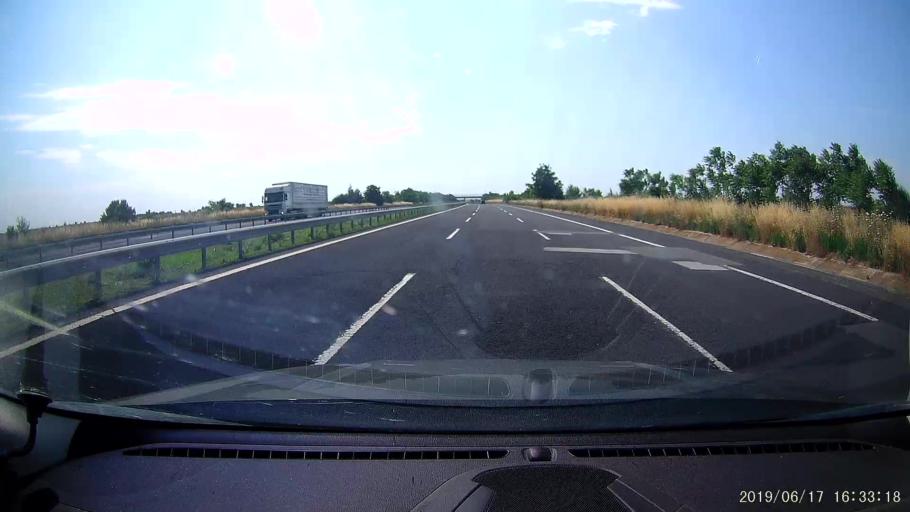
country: TR
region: Kirklareli
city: Buyukkaristiran
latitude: 41.3800
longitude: 27.5771
